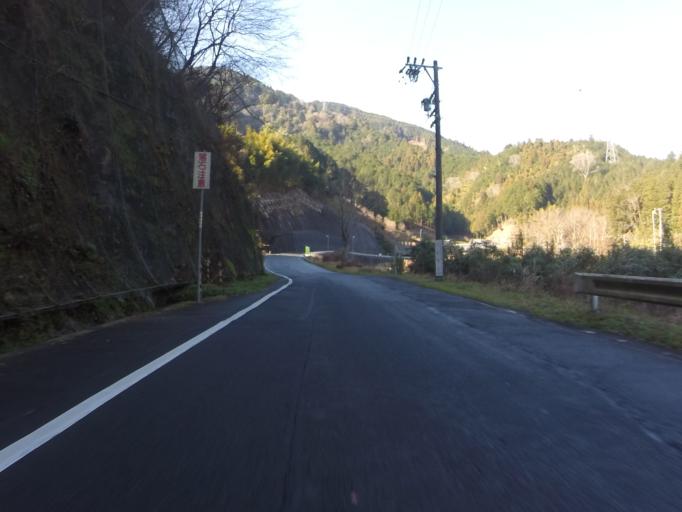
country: JP
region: Shizuoka
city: Fujinomiya
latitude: 35.1255
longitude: 138.4768
